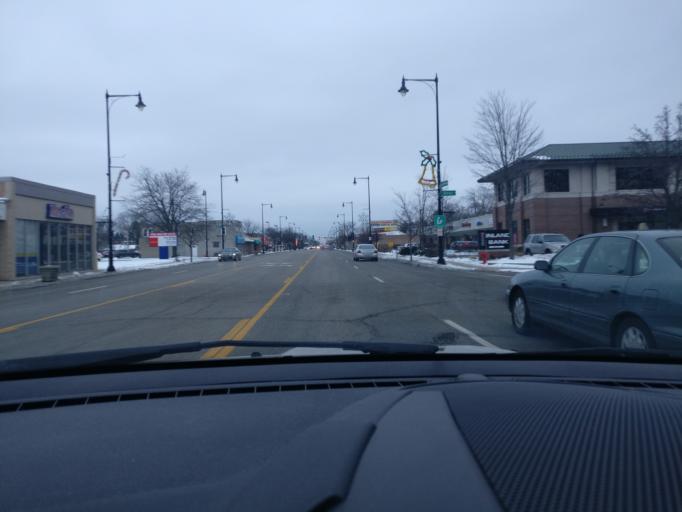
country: US
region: Illinois
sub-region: Cook County
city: Morton Grove
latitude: 42.0409
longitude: -87.7799
